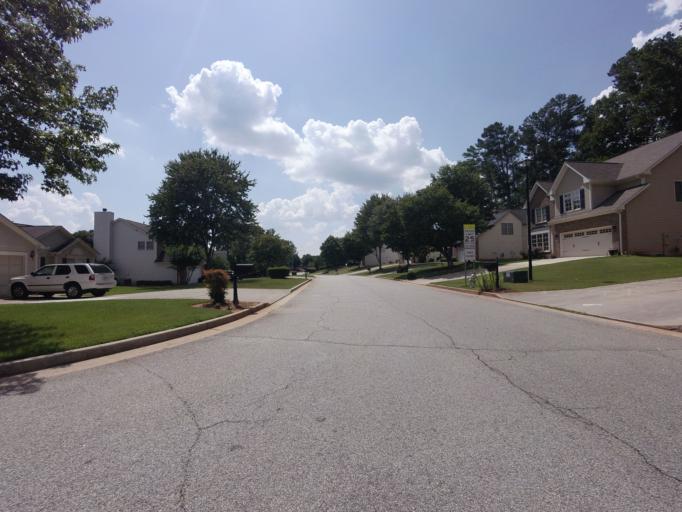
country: US
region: Georgia
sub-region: Fulton County
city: Johns Creek
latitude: 34.0476
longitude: -84.2053
